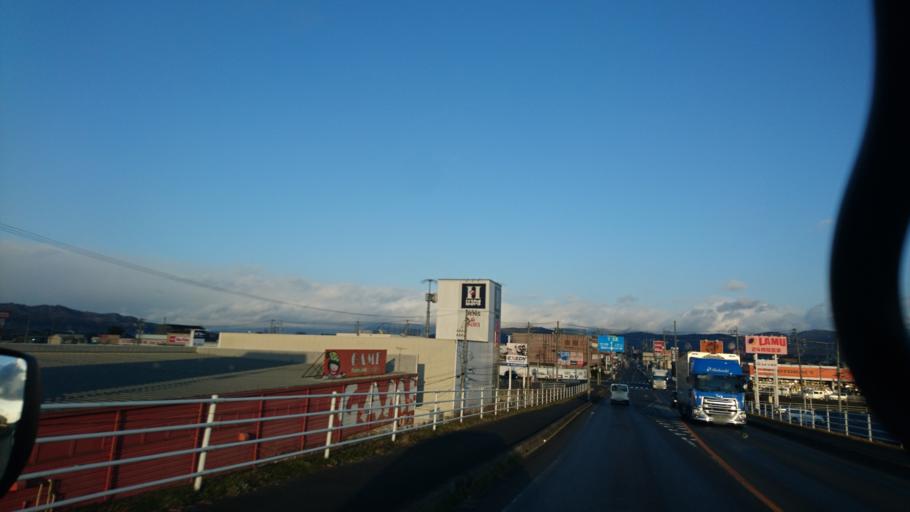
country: JP
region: Mie
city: Ueno-ebisumachi
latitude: 34.7750
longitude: 136.1224
